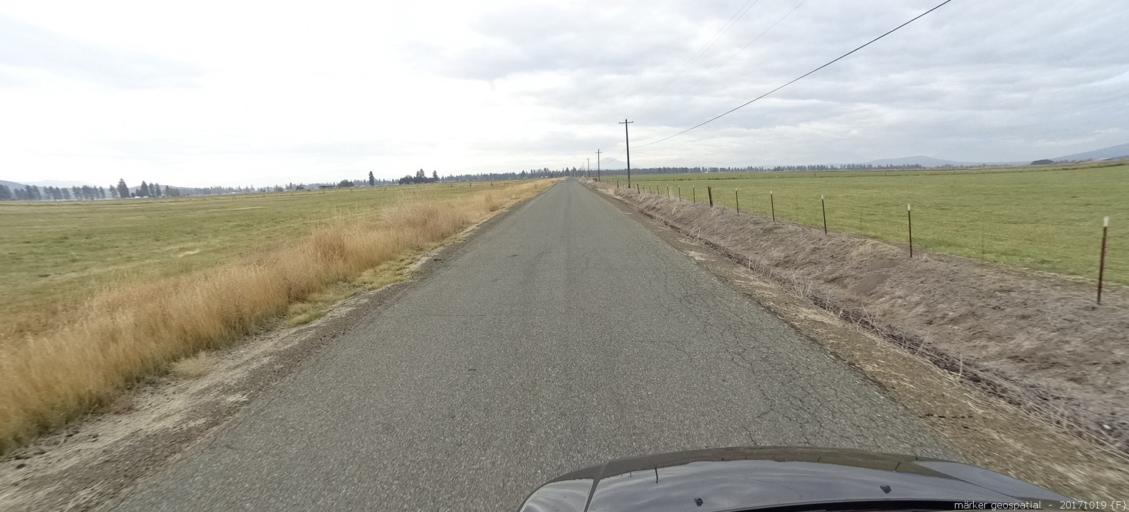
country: US
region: California
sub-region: Shasta County
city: Burney
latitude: 41.0863
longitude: -121.3653
